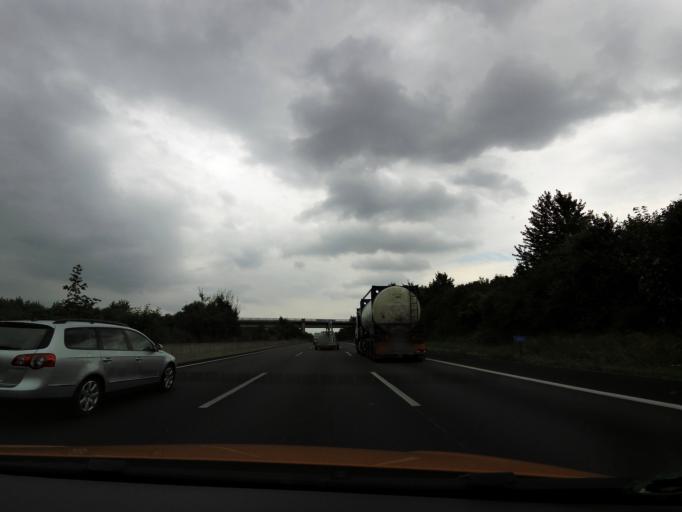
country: DE
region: Lower Saxony
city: Konigslutter am Elm
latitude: 52.3116
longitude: 10.7578
